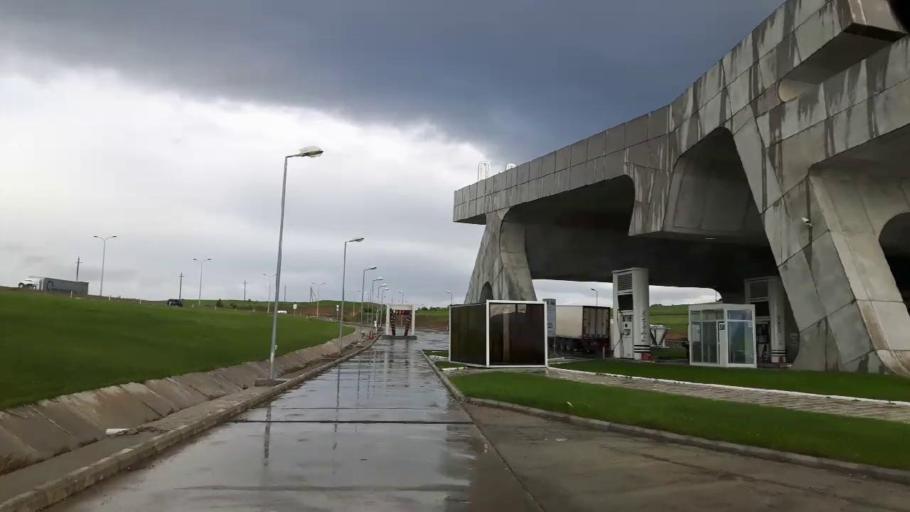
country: GE
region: Shida Kartli
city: Gori
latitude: 42.0157
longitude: 44.0301
